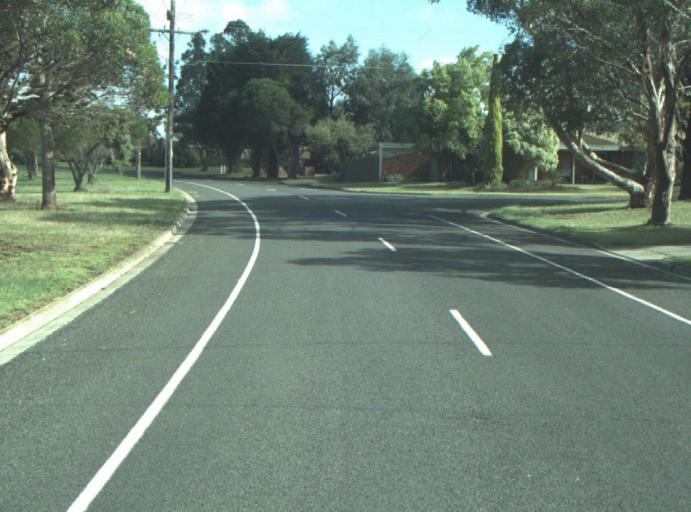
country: AU
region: Victoria
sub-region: Greater Geelong
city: Lara
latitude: -38.0211
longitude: 144.3911
